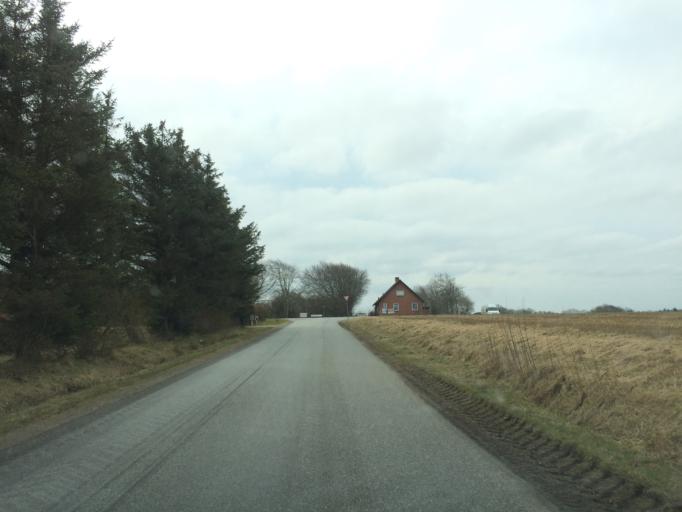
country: DK
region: South Denmark
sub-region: Varde Kommune
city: Oksbol
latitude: 55.7921
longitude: 8.3581
